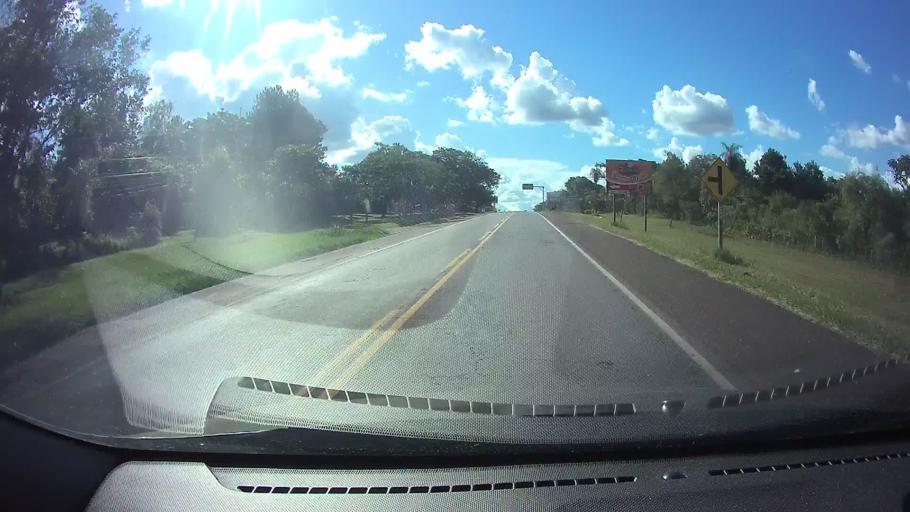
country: PY
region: Cordillera
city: Itacurubi de la Cordillera
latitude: -25.4562
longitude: -56.8944
